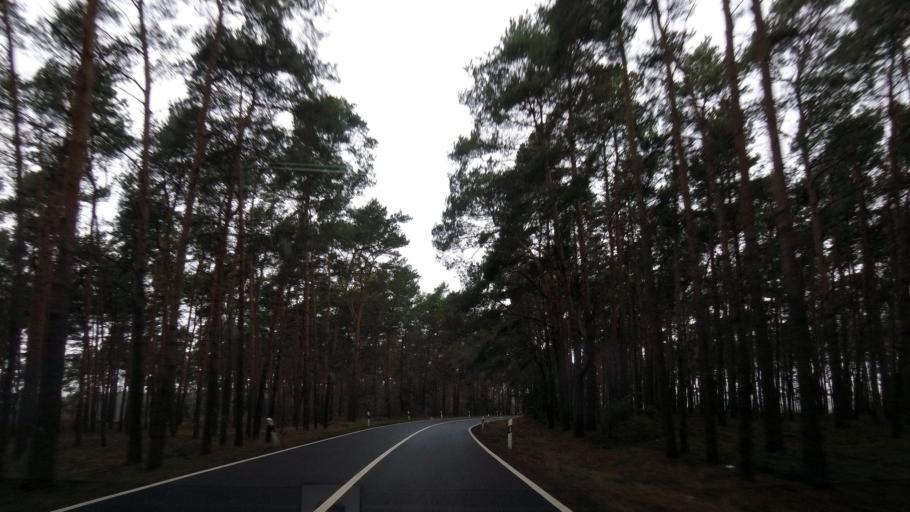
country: DE
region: Brandenburg
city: Treuenbrietzen
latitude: 52.1433
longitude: 12.9562
